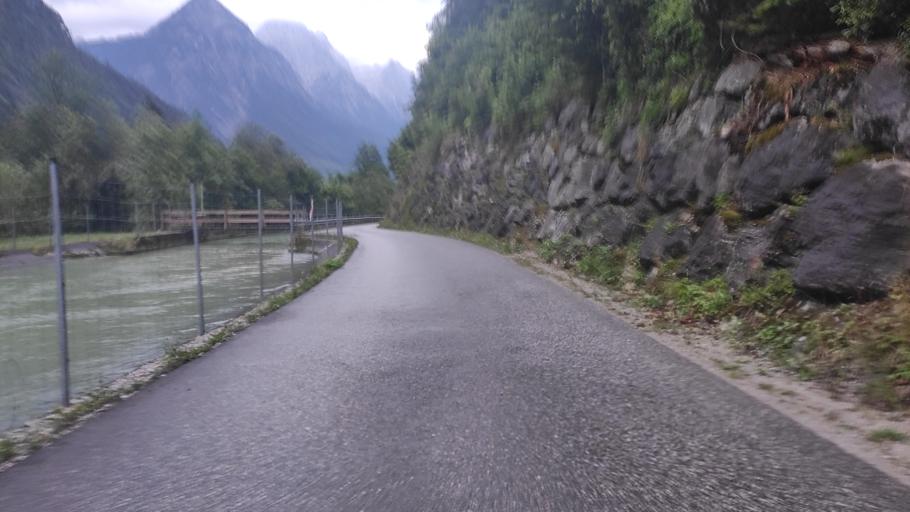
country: AT
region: Salzburg
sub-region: Politischer Bezirk Zell am See
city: Sankt Martin bei Lofer
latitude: 47.5541
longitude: 12.7231
